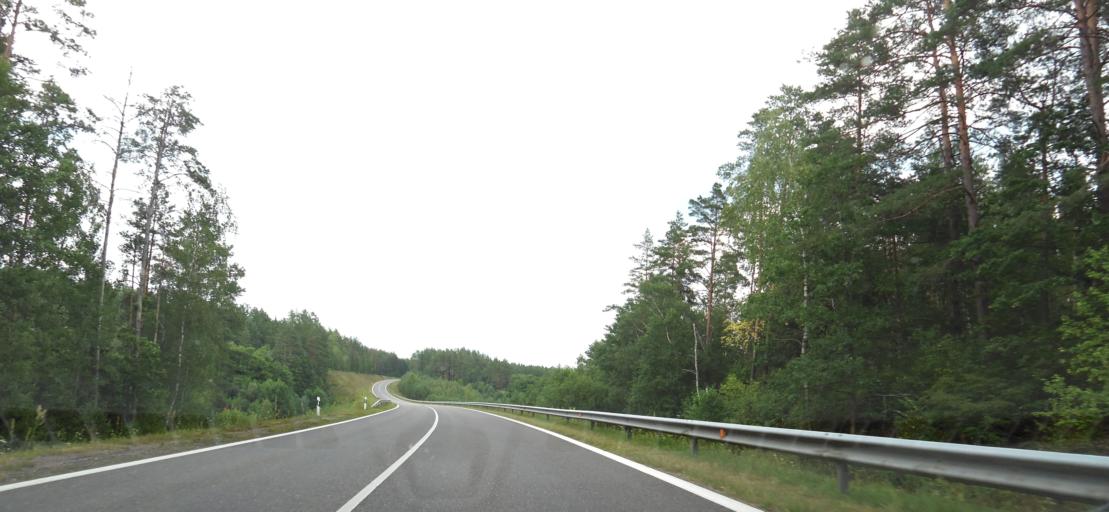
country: LT
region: Alytaus apskritis
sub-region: Alytaus rajonas
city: Daugai
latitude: 54.1998
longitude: 24.3693
